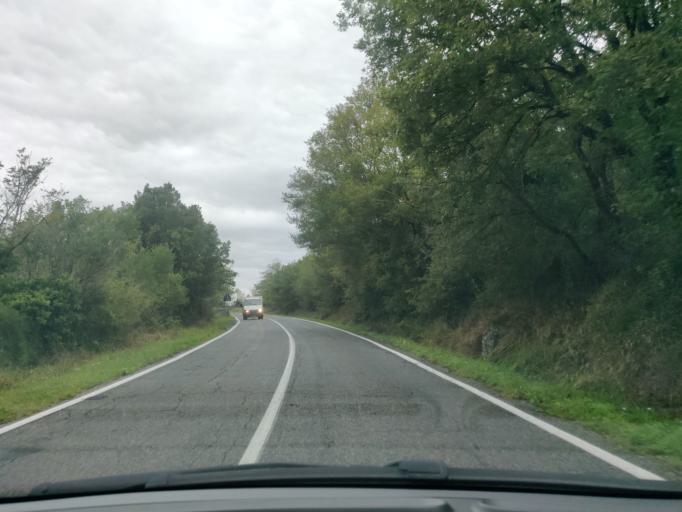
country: IT
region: Latium
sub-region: Citta metropolitana di Roma Capitale
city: Allumiere
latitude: 42.1461
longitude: 11.8965
